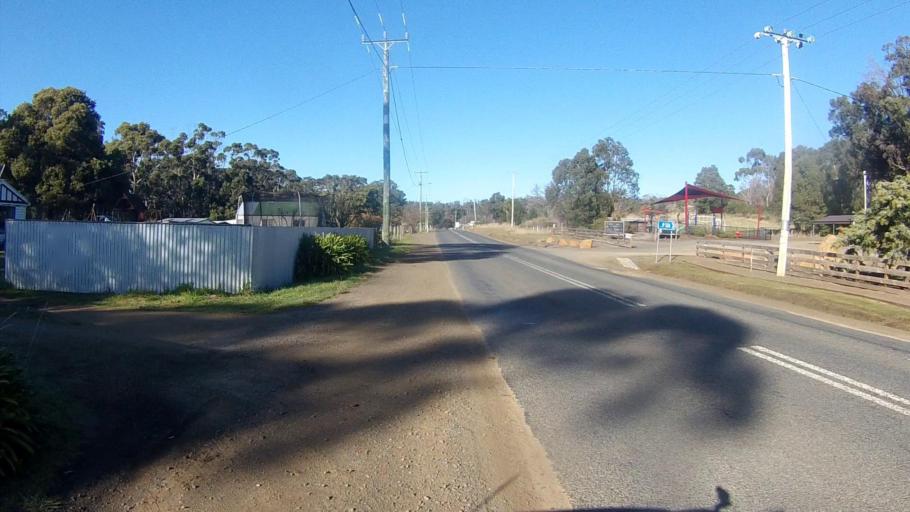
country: AU
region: Tasmania
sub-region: Sorell
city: Sorell
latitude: -42.9458
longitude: 147.8657
